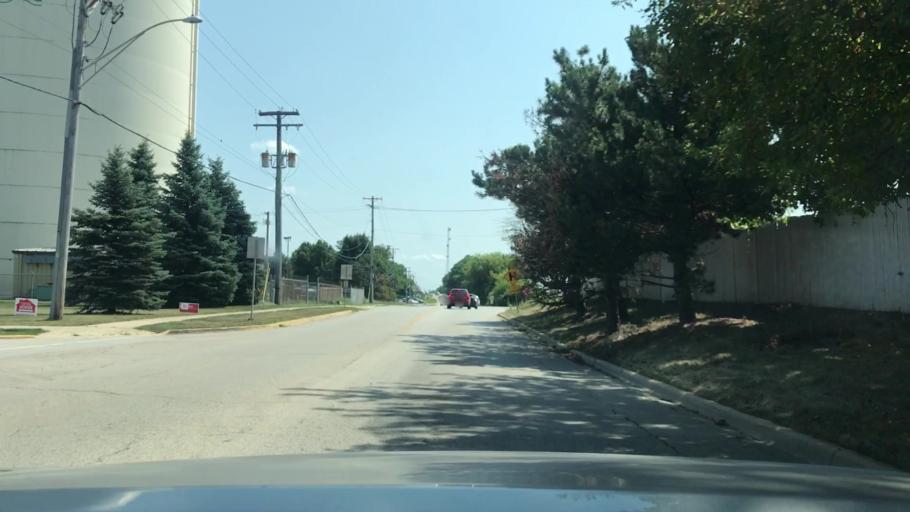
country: US
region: Illinois
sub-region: Kane County
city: Aurora
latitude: 41.7259
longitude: -88.2353
